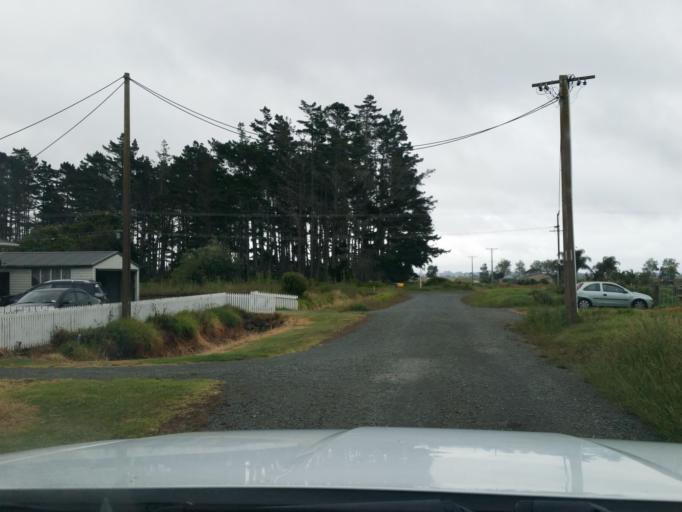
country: NZ
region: Northland
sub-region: Kaipara District
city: Dargaville
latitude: -36.0142
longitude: 173.9053
